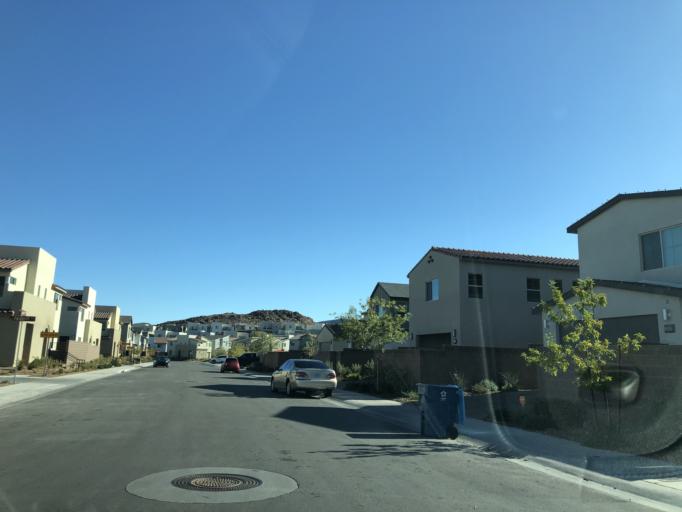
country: US
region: Nevada
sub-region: Clark County
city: Whitney
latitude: 35.9998
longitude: -115.0866
